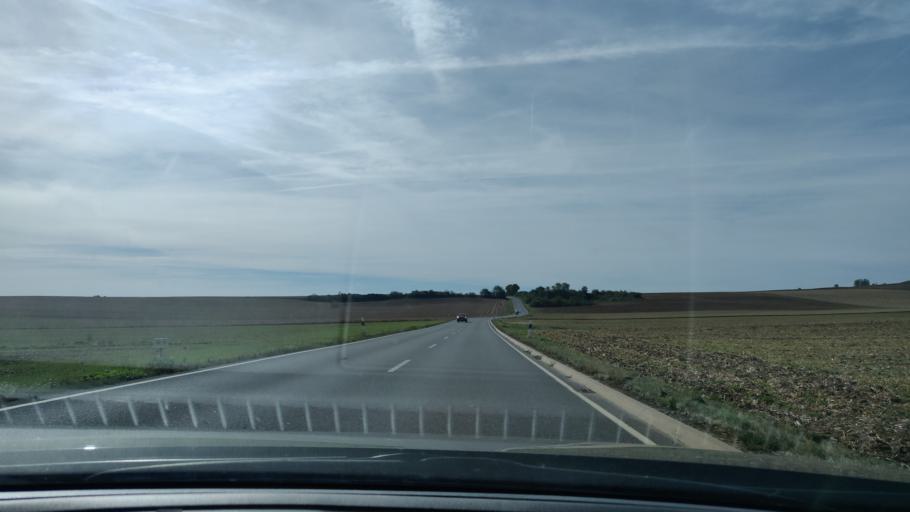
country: DE
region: Hesse
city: Fritzlar
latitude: 51.1539
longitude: 9.2745
